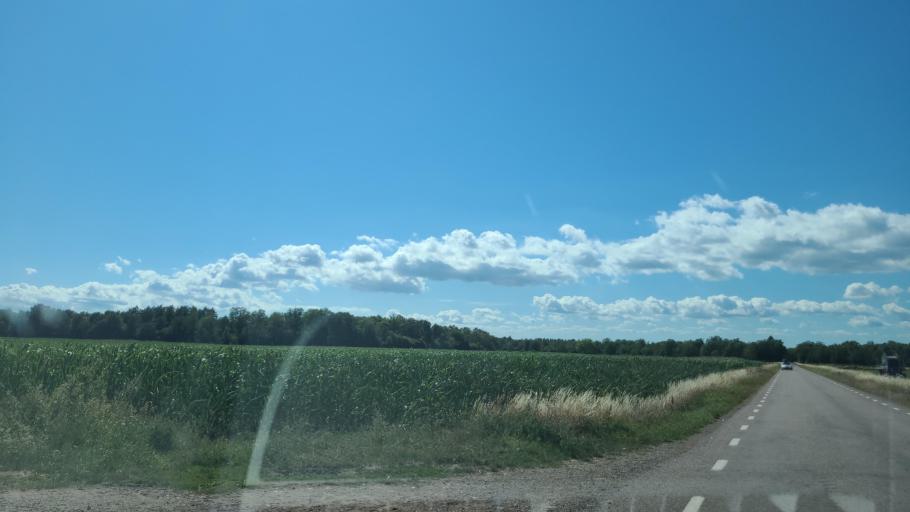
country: SE
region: Kalmar
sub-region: Borgholms Kommun
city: Borgholm
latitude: 56.7807
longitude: 16.7180
